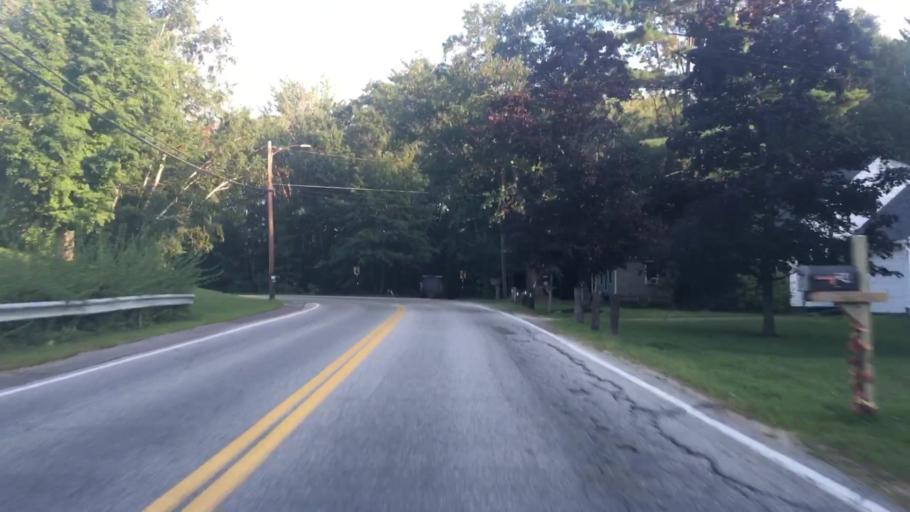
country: US
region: New Hampshire
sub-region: Belknap County
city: Laconia
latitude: 43.5149
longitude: -71.4580
